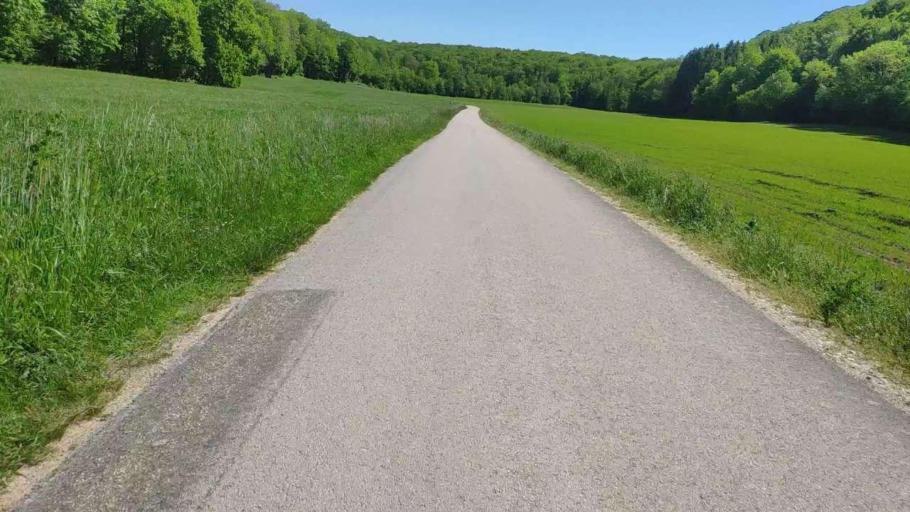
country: FR
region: Franche-Comte
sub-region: Departement du Jura
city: Poligny
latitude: 46.7399
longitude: 5.7700
